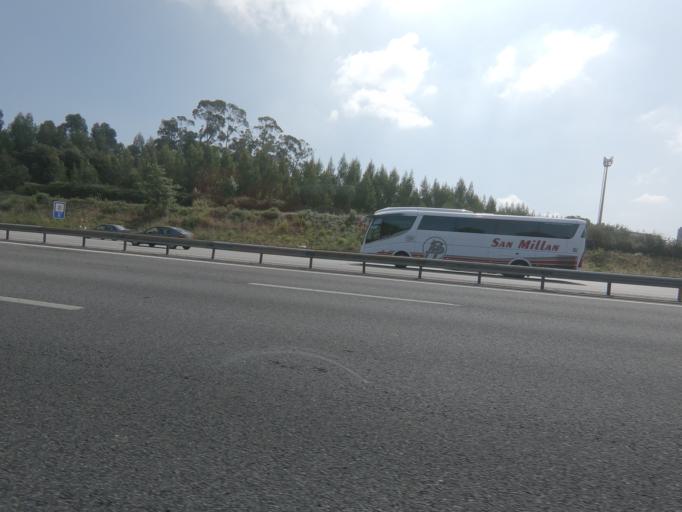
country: PT
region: Porto
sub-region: Maia
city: Pedroucos
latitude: 41.1785
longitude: -8.5934
